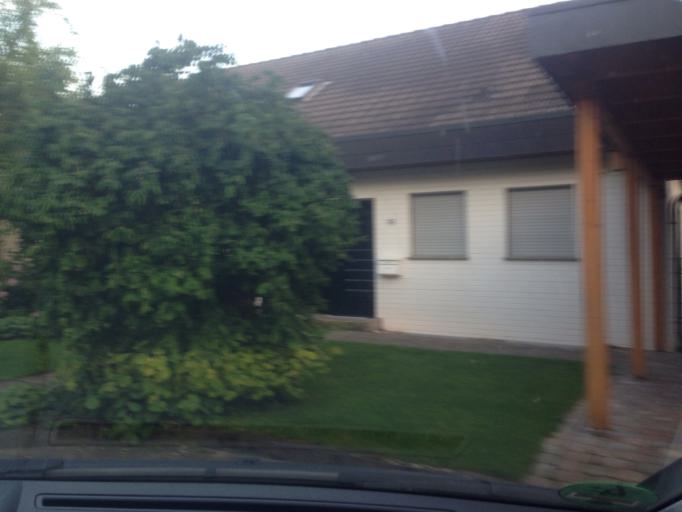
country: DE
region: North Rhine-Westphalia
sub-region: Regierungsbezirk Munster
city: Greven
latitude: 52.0233
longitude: 7.5626
